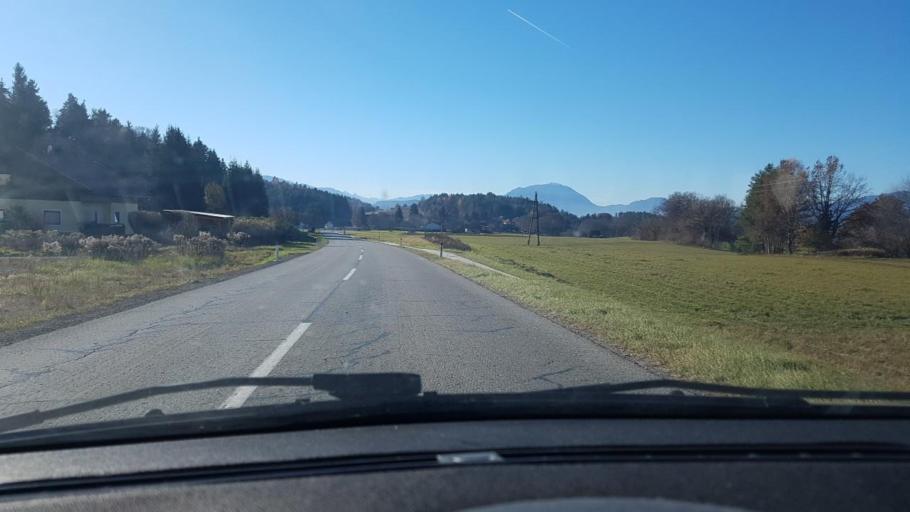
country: AT
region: Carinthia
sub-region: Politischer Bezirk Klagenfurt Land
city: Schiefling am See
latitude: 46.6006
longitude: 14.0761
